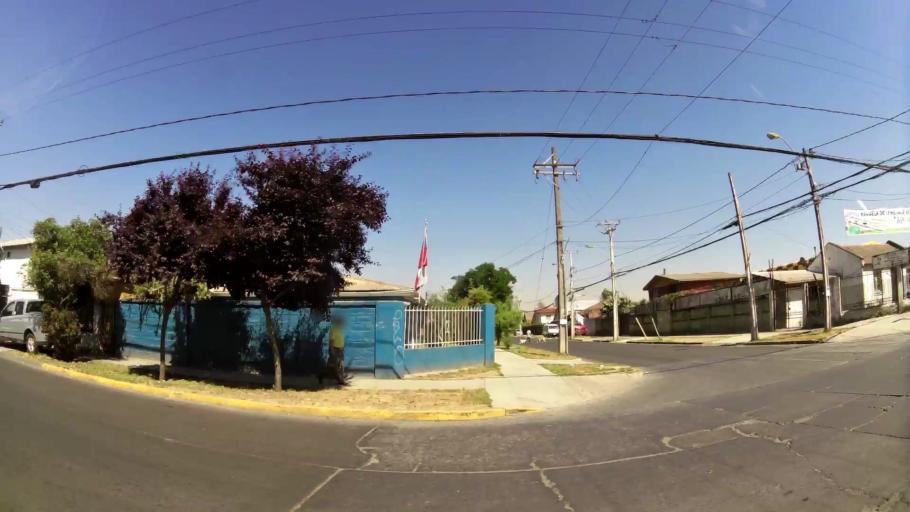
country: CL
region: Santiago Metropolitan
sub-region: Provincia de Santiago
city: La Pintana
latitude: -33.5488
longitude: -70.6595
